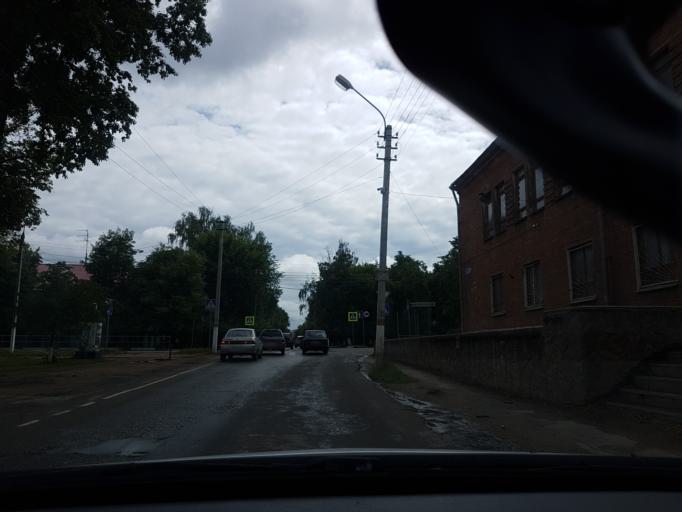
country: RU
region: Moskovskaya
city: Istra
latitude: 55.9209
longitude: 36.8615
